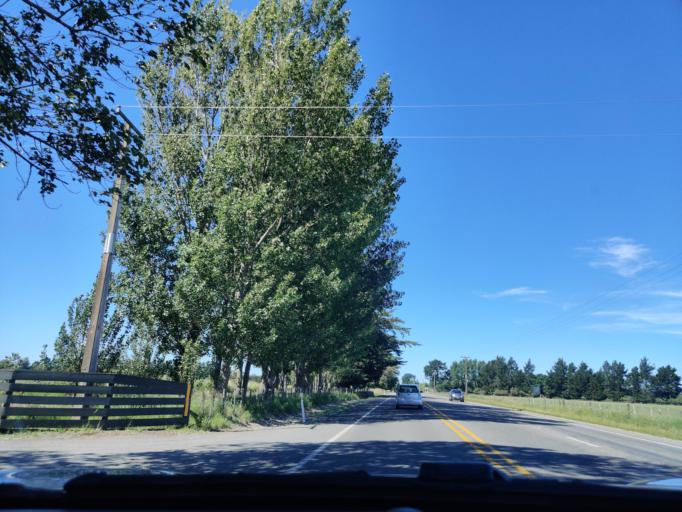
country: NZ
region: Wellington
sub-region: Masterton District
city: Masterton
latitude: -41.0950
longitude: 175.4374
